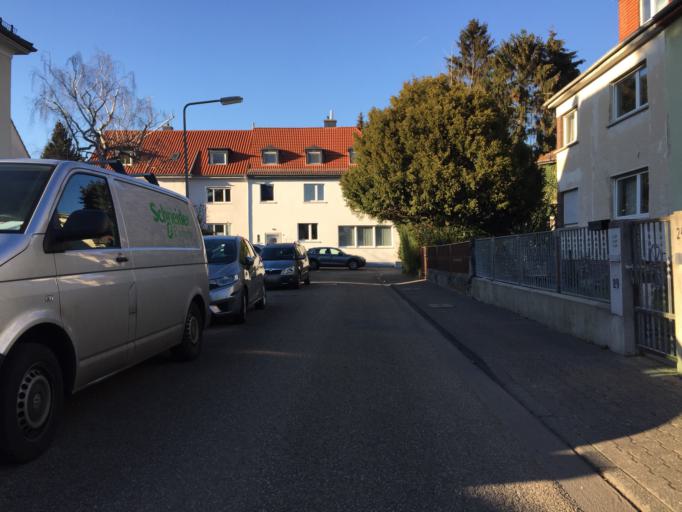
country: DE
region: Hesse
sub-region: Regierungsbezirk Darmstadt
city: Frankfurt am Main
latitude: 50.1550
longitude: 8.6688
